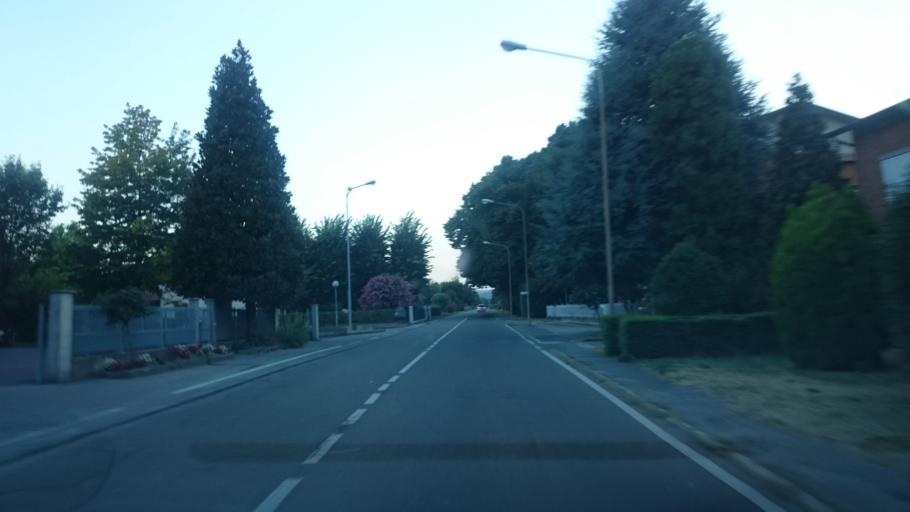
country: IT
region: Emilia-Romagna
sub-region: Provincia di Reggio Emilia
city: Arceto
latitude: 44.6162
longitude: 10.7189
